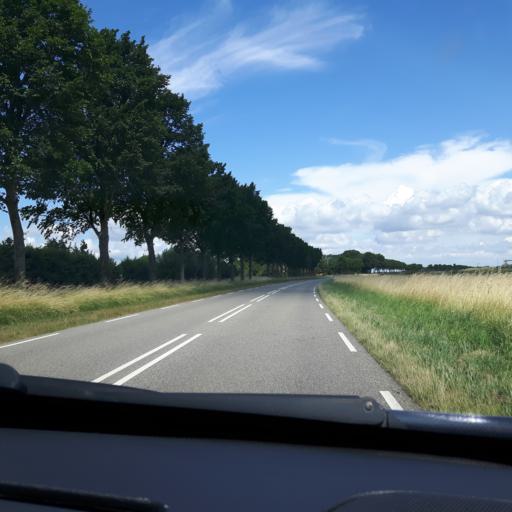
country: NL
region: Zeeland
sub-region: Gemeente Goes
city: Goes
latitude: 51.5664
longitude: 3.8672
